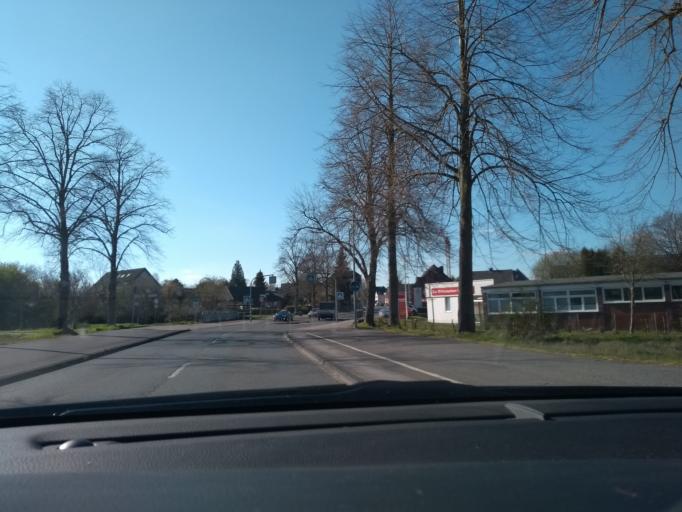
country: DE
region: North Rhine-Westphalia
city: Lunen
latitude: 51.6258
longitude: 7.4978
